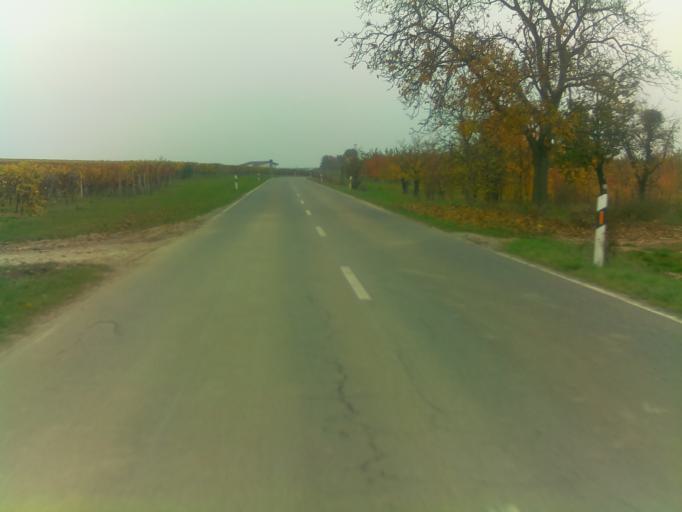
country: DE
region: Rheinland-Pfalz
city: Gonnheim
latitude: 49.4546
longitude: 8.2488
